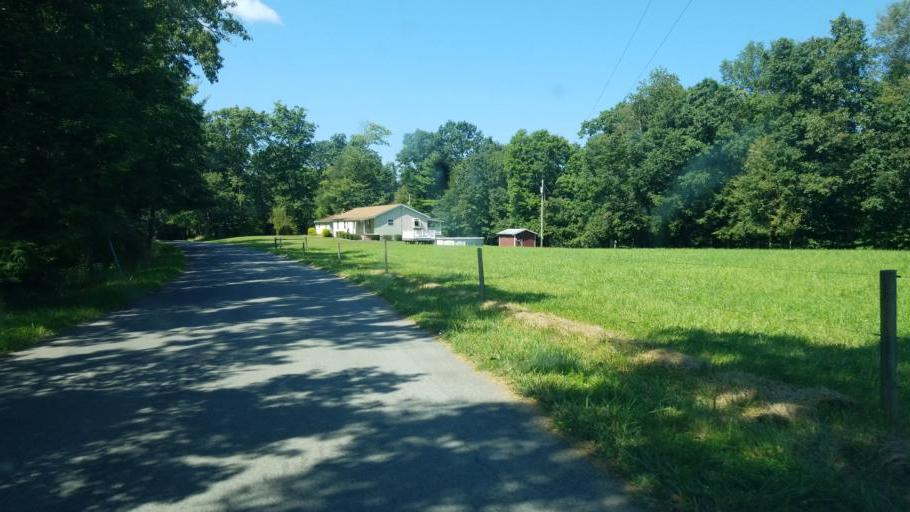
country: US
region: Pennsylvania
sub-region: Clarion County
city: Clarion
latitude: 41.1733
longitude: -79.4217
